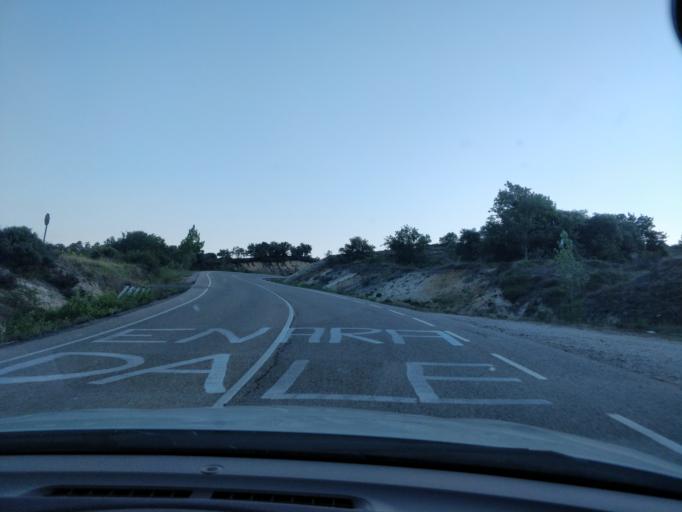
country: ES
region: Castille and Leon
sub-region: Provincia de Burgos
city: Medina de Pomar
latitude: 42.9954
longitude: -3.5276
